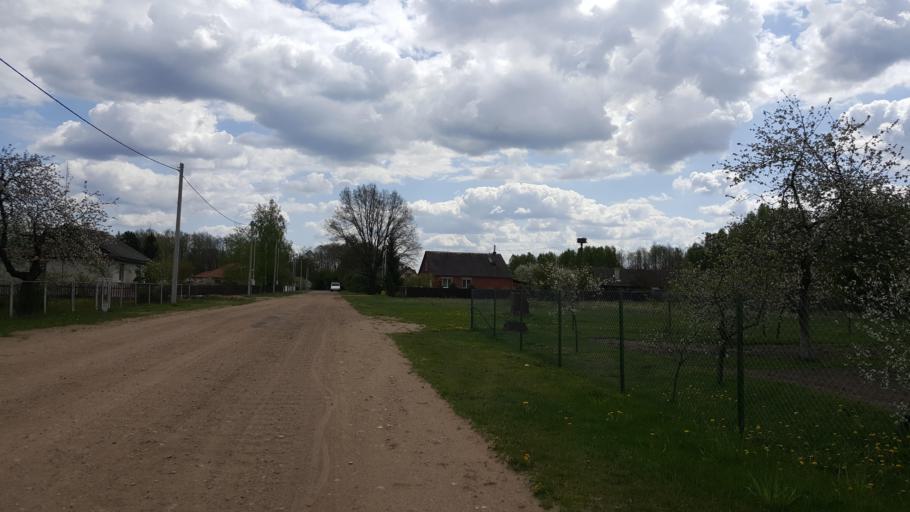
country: BY
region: Brest
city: Zhabinka
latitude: 52.3933
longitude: 24.0090
